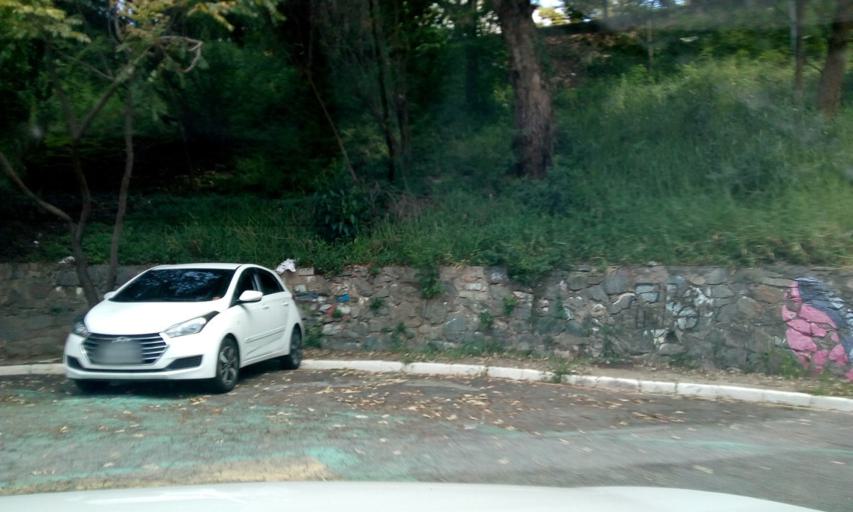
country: BR
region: Sao Paulo
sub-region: Sao Paulo
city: Sao Paulo
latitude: -23.5315
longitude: -46.7090
